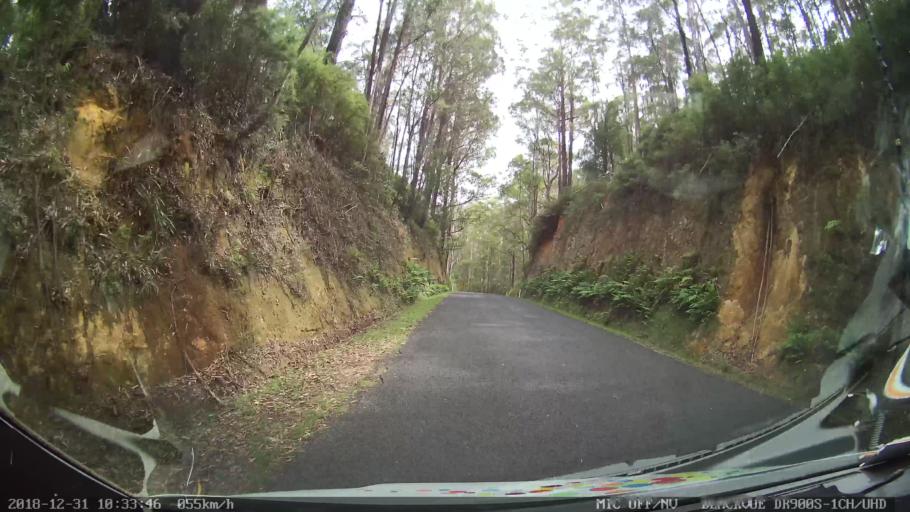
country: AU
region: New South Wales
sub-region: Snowy River
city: Jindabyne
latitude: -36.4452
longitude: 148.1666
